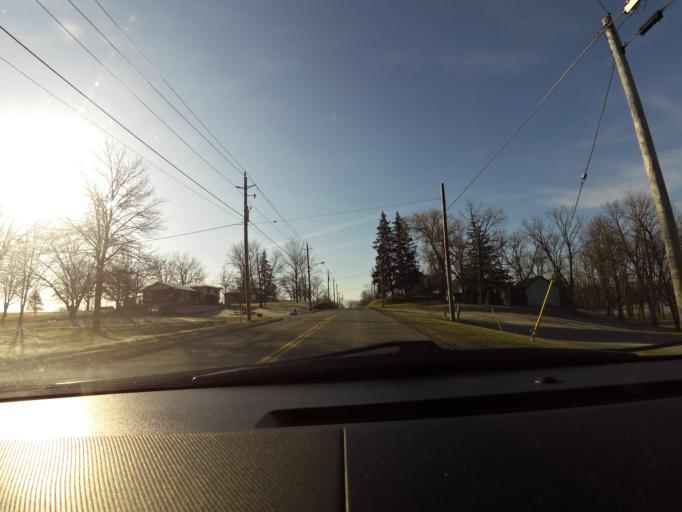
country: CA
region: Ontario
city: Ancaster
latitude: 43.0197
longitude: -79.8897
